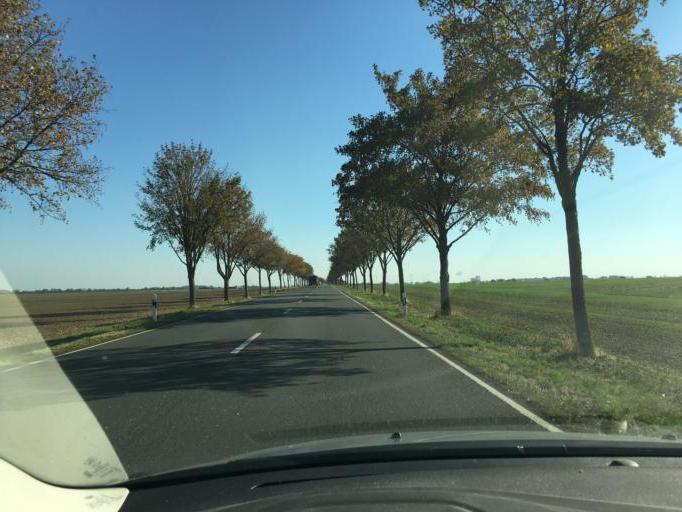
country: DE
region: Saxony-Anhalt
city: Wanzleben
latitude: 52.0222
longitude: 11.4949
